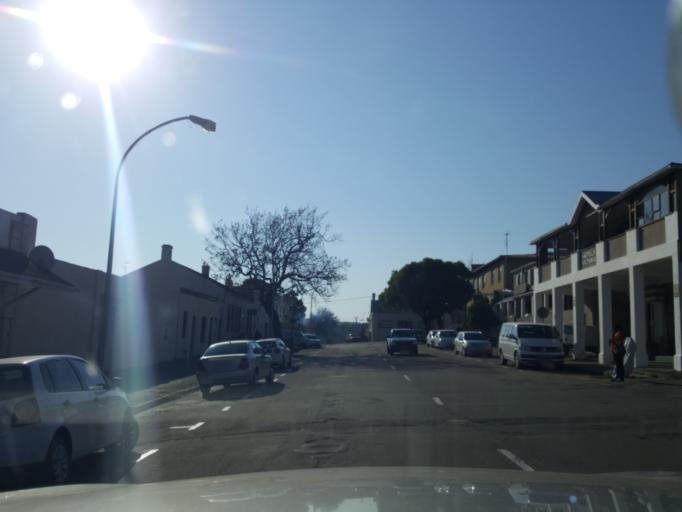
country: ZA
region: Eastern Cape
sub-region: Cacadu District Municipality
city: Grahamstown
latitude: -33.3094
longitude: 26.5246
